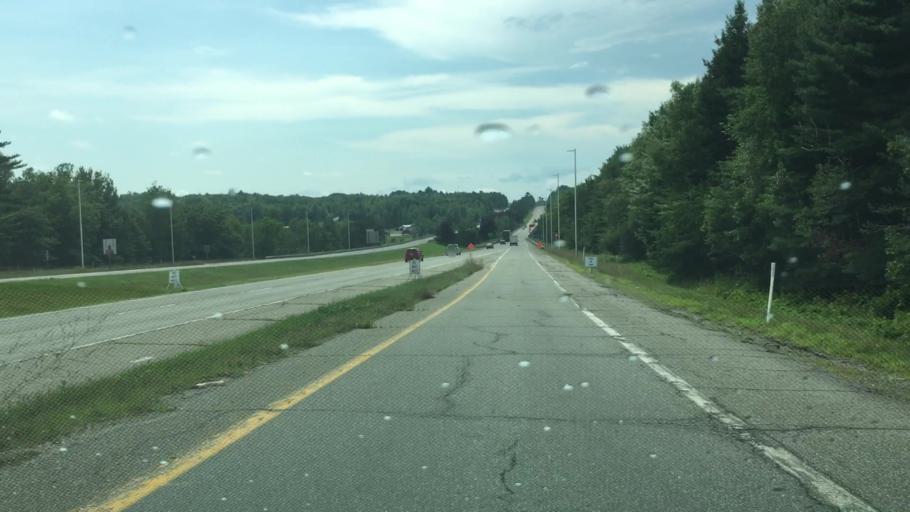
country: US
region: Maine
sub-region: Penobscot County
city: Medway
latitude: 45.6062
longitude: -68.5240
